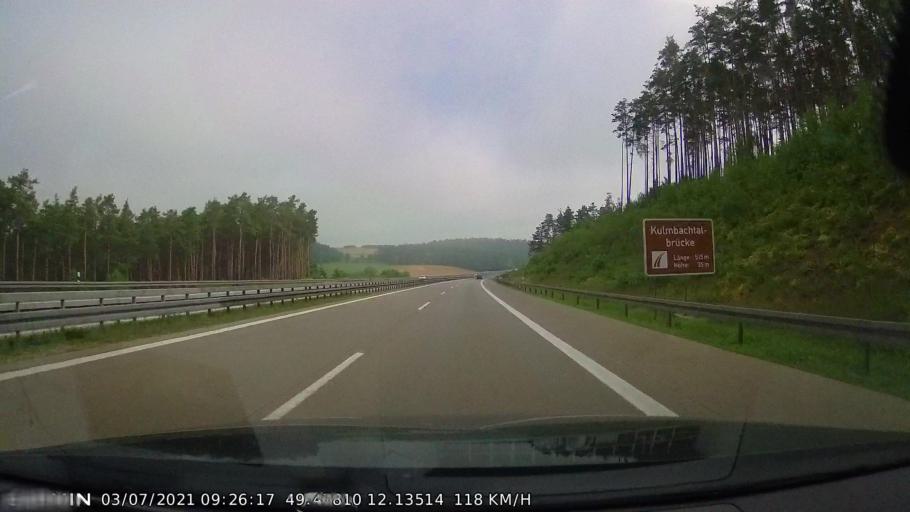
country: DE
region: Bavaria
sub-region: Upper Palatinate
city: Pfreimd
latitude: 49.4784
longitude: 12.1352
